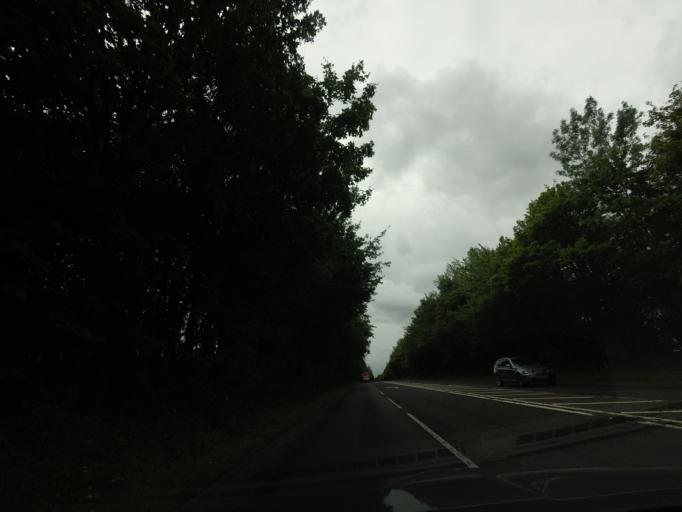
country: GB
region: England
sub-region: Kent
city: East Peckham
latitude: 51.2460
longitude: 0.3753
